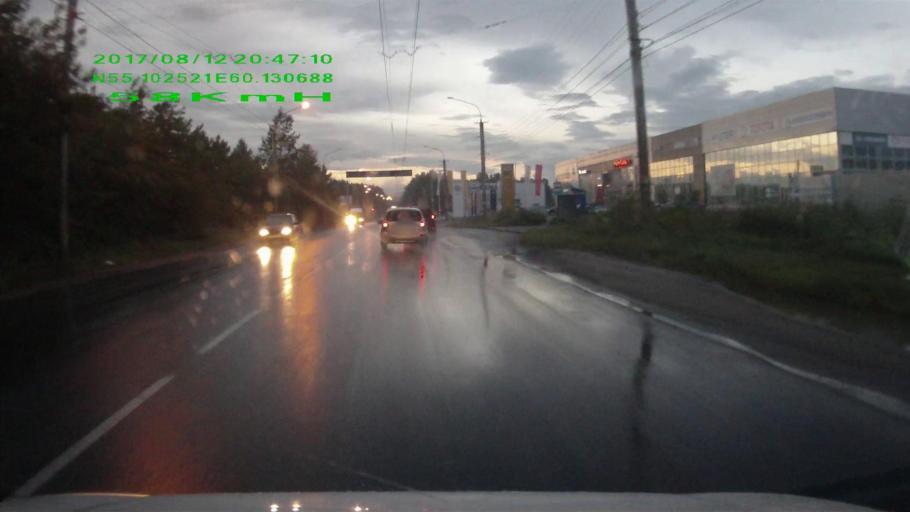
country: RU
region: Chelyabinsk
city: Turgoyak
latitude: 55.1029
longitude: 60.1307
